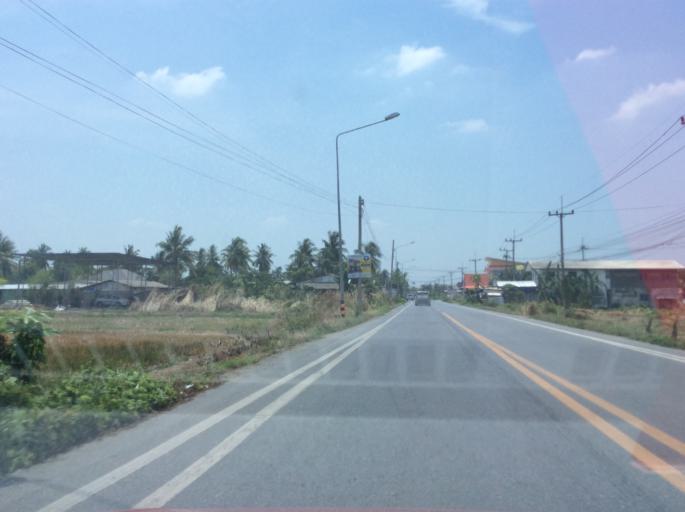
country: TH
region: Pathum Thani
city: Ban Lam Luk Ka
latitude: 13.9884
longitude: 100.7777
